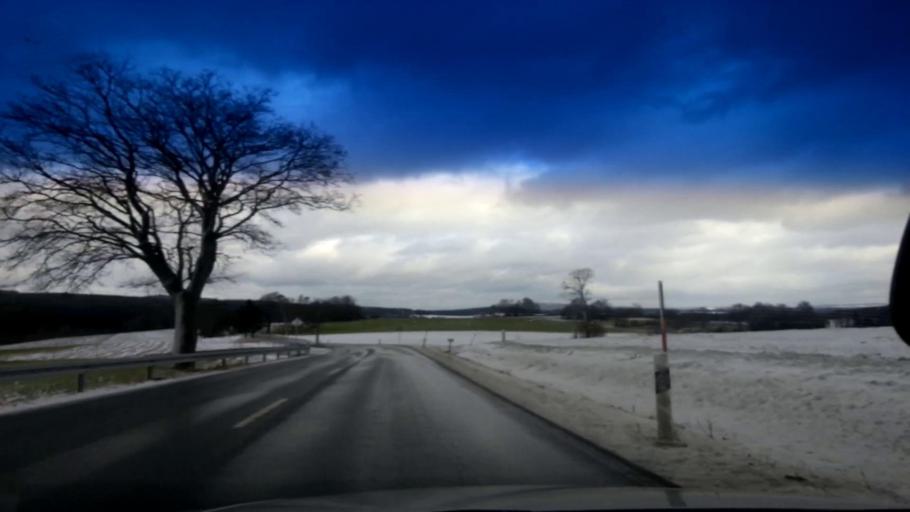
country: DE
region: Bavaria
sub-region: Upper Franconia
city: Weissenstadt
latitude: 50.1117
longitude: 11.8967
